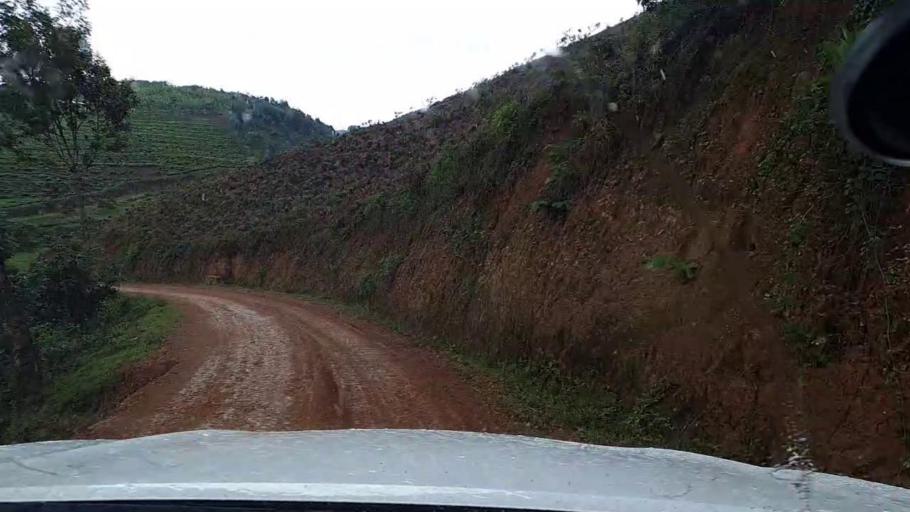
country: RW
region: Western Province
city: Kibuye
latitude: -2.1611
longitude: 29.4353
